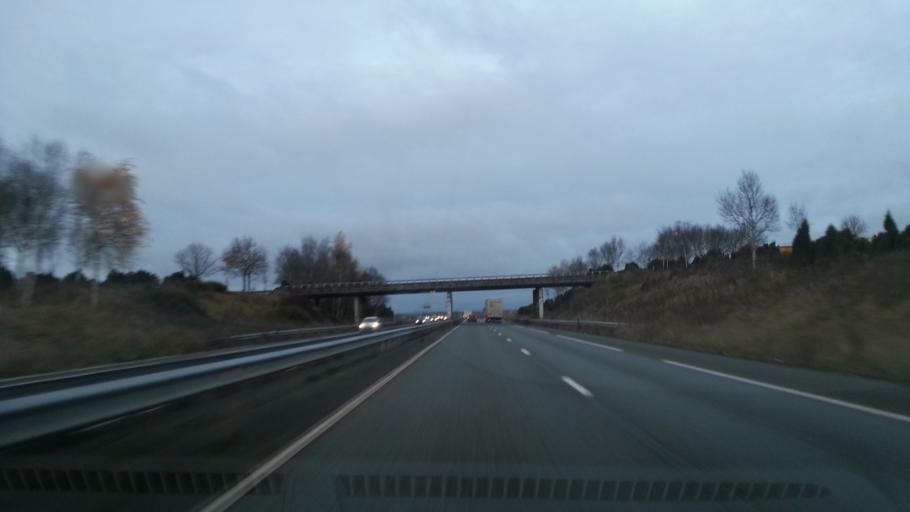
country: FR
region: Picardie
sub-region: Departement de l'Oise
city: Bresles
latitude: 49.4144
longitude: 2.3046
